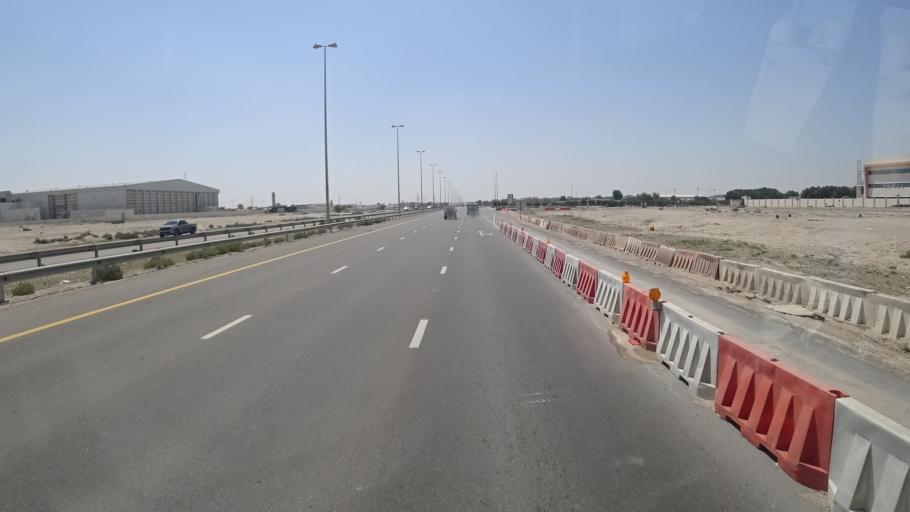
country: AE
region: Abu Dhabi
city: Abu Dhabi
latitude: 24.3117
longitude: 54.6756
